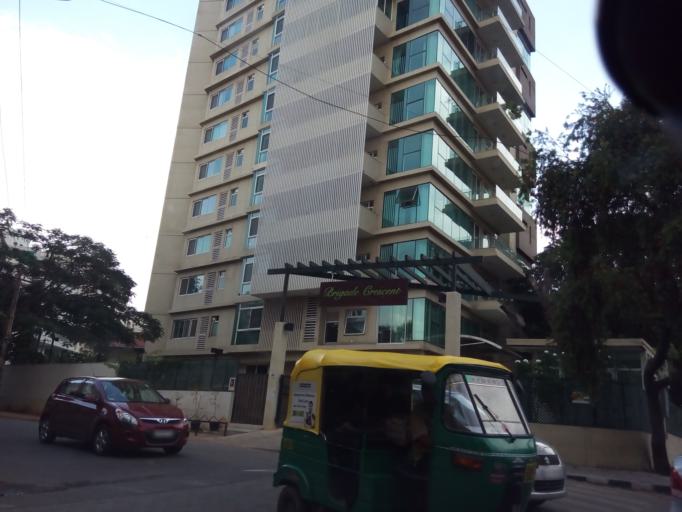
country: IN
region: Karnataka
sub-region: Bangalore Urban
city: Bangalore
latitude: 12.9993
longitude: 77.6001
